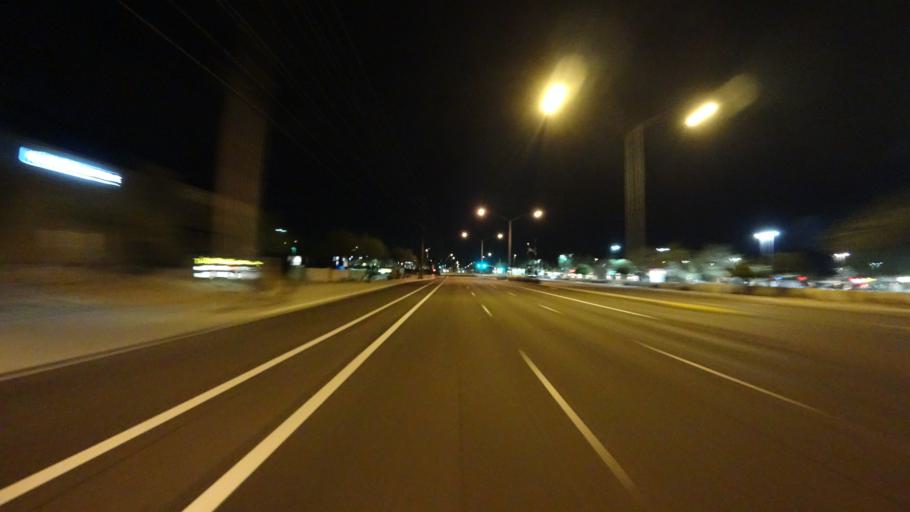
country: US
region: Arizona
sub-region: Pinal County
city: Apache Junction
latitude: 33.4680
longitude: -111.6838
